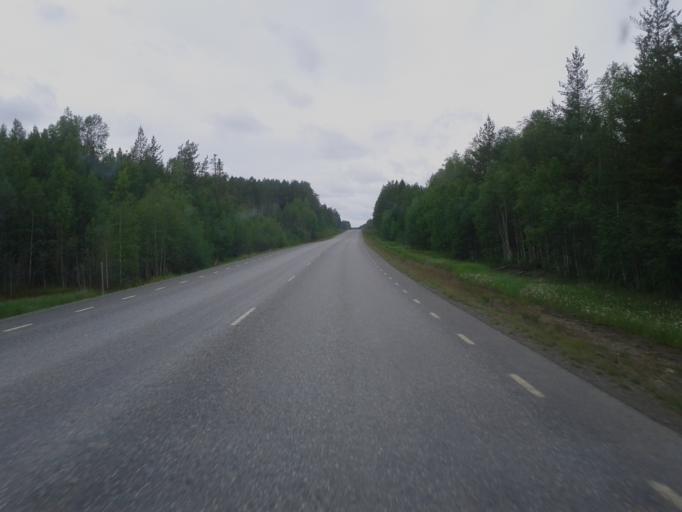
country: SE
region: Vaesterbotten
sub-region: Skelleftea Kommun
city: Boliden
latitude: 64.8773
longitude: 20.3276
